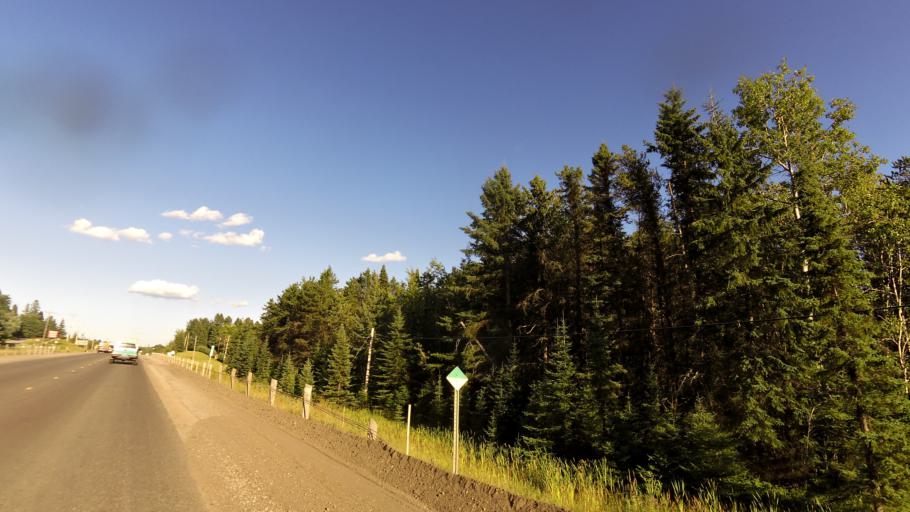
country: CA
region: Ontario
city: Dryden
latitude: 49.8151
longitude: -92.8680
